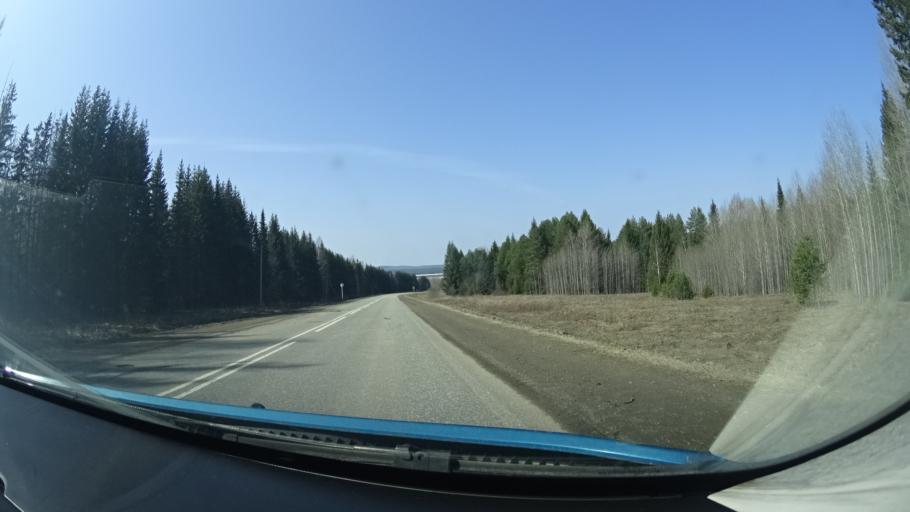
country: RU
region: Perm
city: Osa
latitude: 57.3253
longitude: 55.6051
